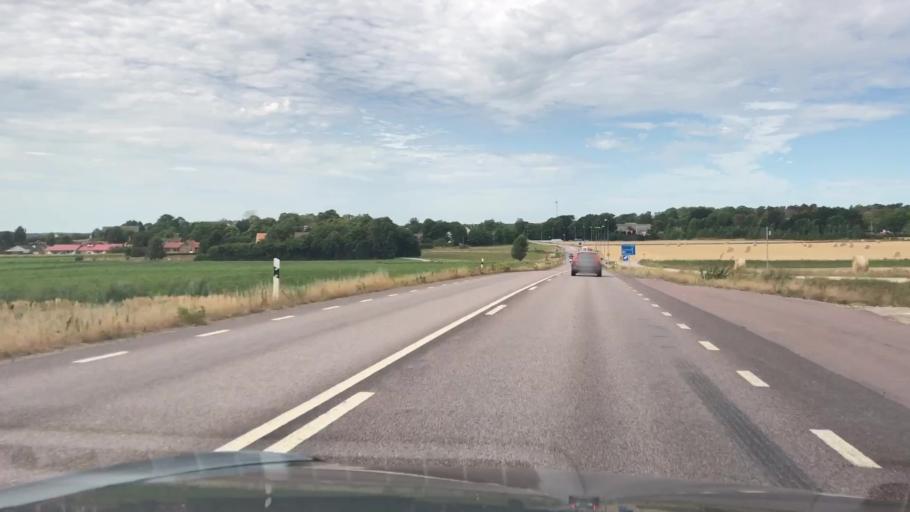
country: SE
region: Blekinge
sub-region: Karlskrona Kommun
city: Jaemjoe
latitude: 56.1840
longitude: 15.7762
